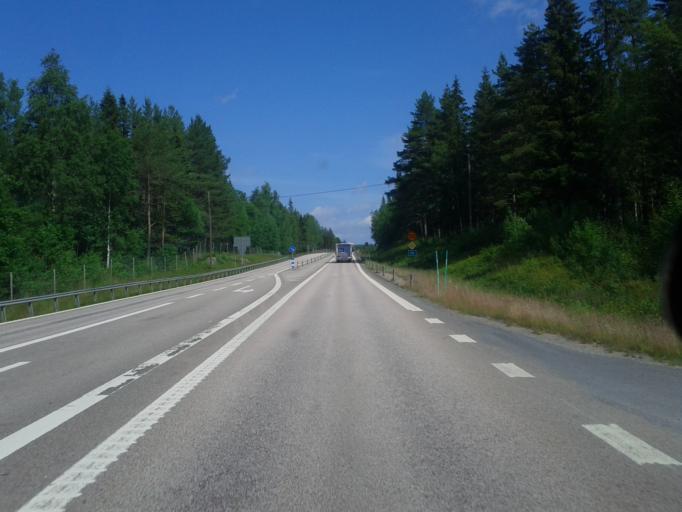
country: SE
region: Vaesterbotten
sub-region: Nordmalings Kommun
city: Nordmaling
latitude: 63.5118
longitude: 19.3582
